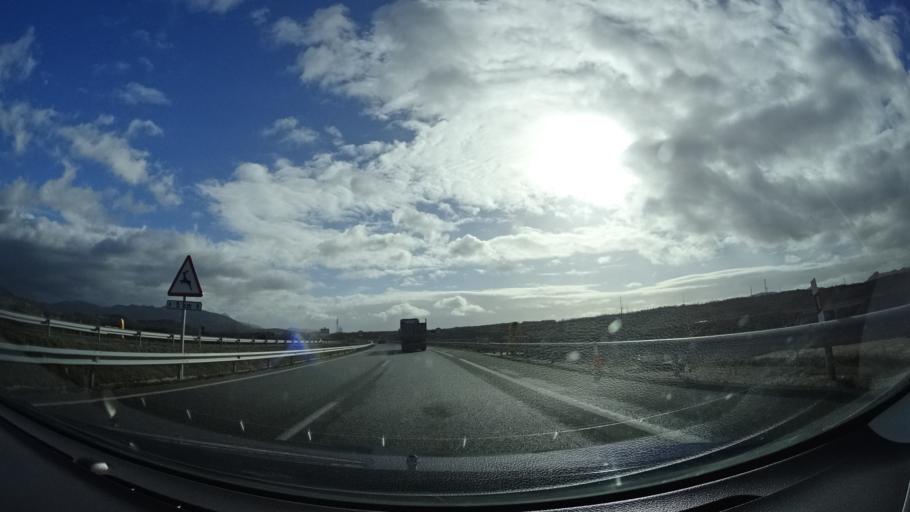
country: ES
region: Basque Country
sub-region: Provincia de Alava
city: Arminon
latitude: 42.7028
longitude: -2.9005
